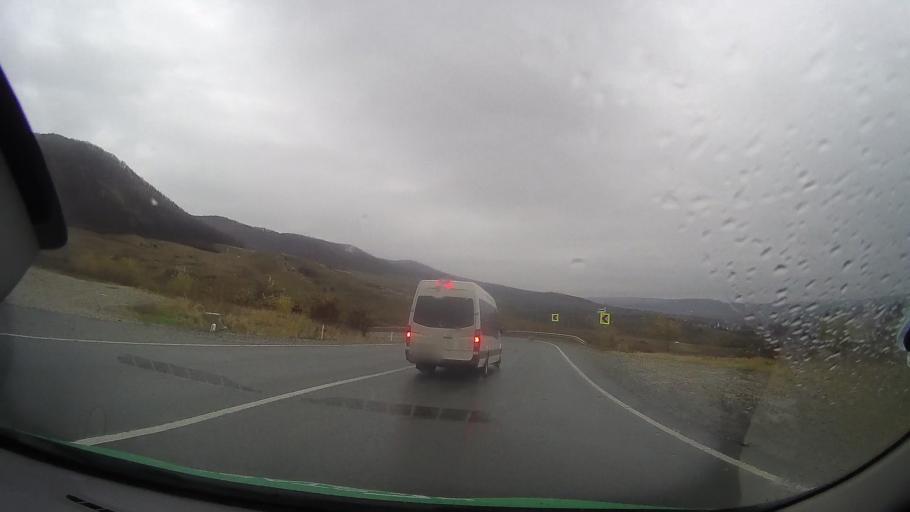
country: RO
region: Bistrita-Nasaud
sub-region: Comuna Galatii Bistritei
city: Galatii Bistritei
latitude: 47.0317
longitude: 24.4225
